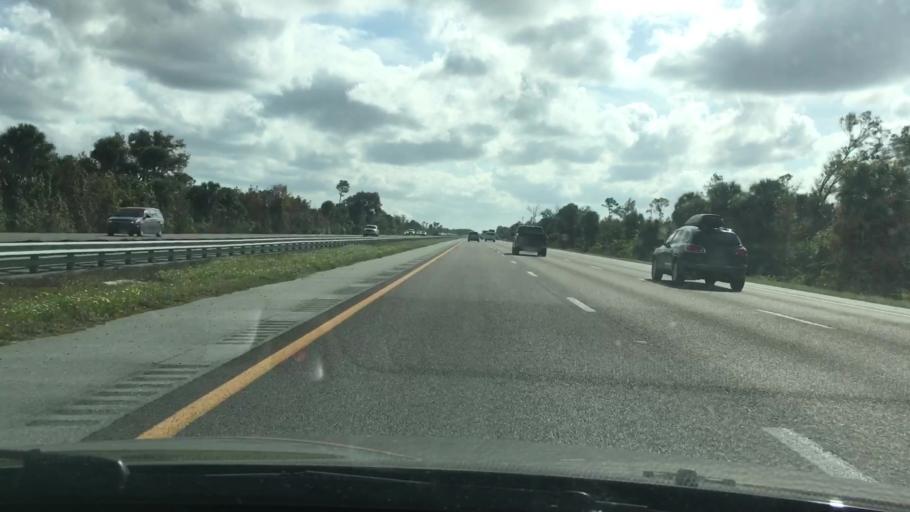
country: US
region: Florida
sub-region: Volusia County
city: Oak Hill
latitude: 28.8143
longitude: -80.9063
